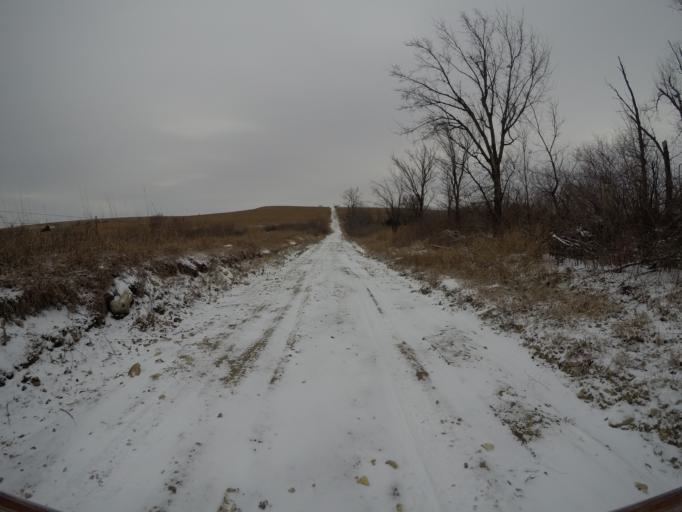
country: US
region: Kansas
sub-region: Wabaunsee County
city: Alma
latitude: 38.8802
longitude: -96.1136
